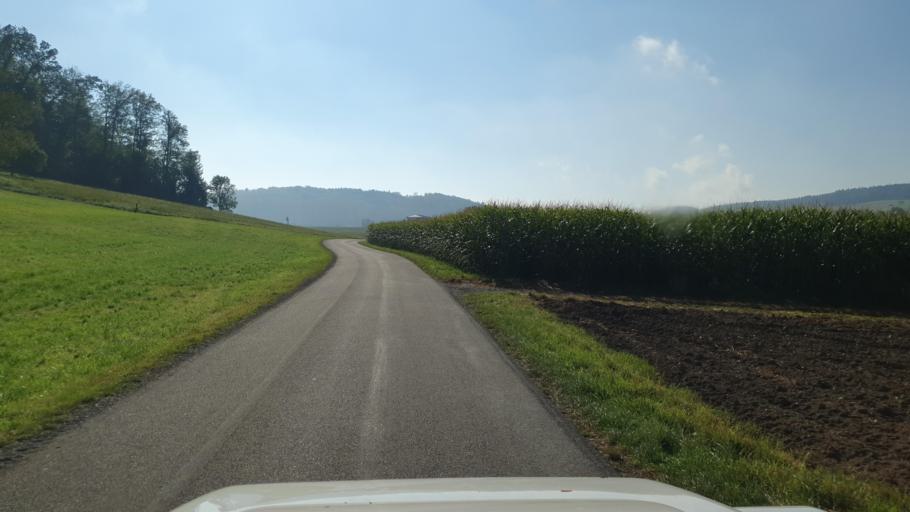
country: CH
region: Aargau
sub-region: Bezirk Bremgarten
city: Villmergen
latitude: 47.3325
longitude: 8.2605
